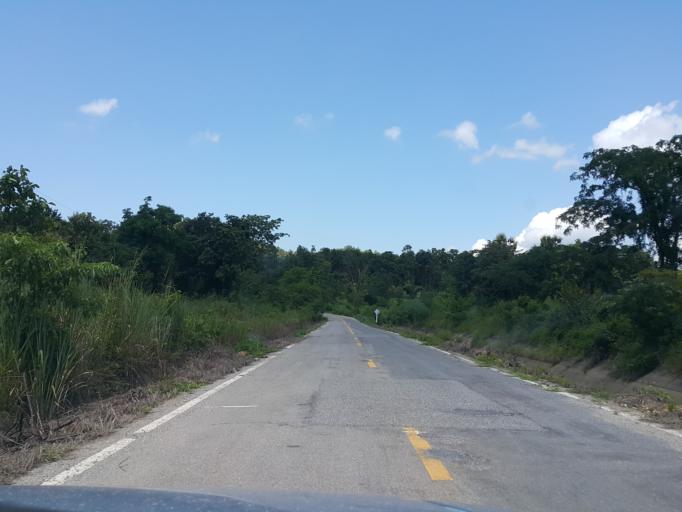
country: TH
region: Chiang Mai
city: San Kamphaeng
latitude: 18.7002
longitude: 99.1784
